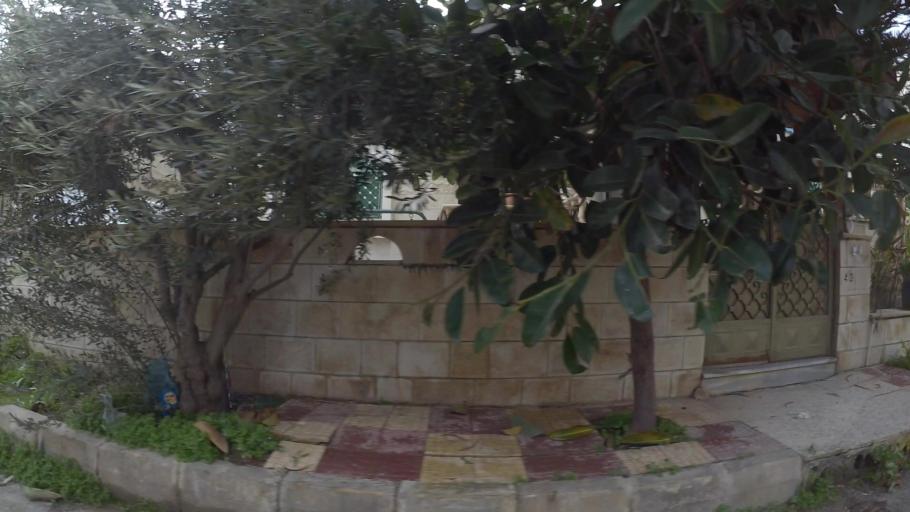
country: JO
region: Amman
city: Al Jubayhah
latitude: 32.0612
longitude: 35.8272
